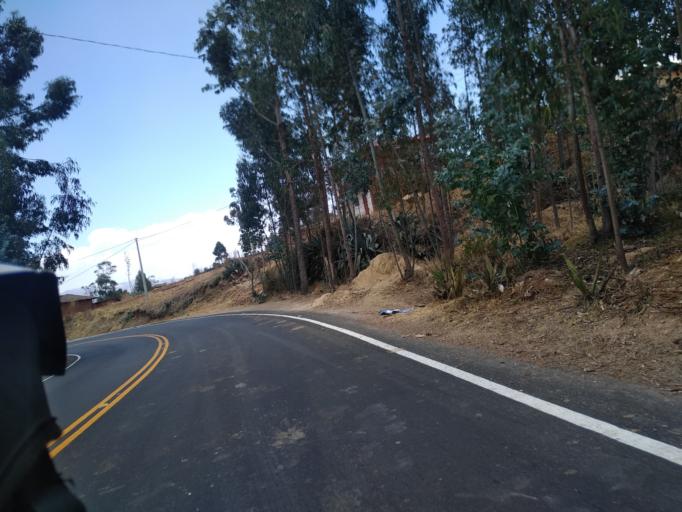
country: PE
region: Cajamarca
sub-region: San Marcos
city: San Marcos
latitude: -7.2778
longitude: -78.2391
